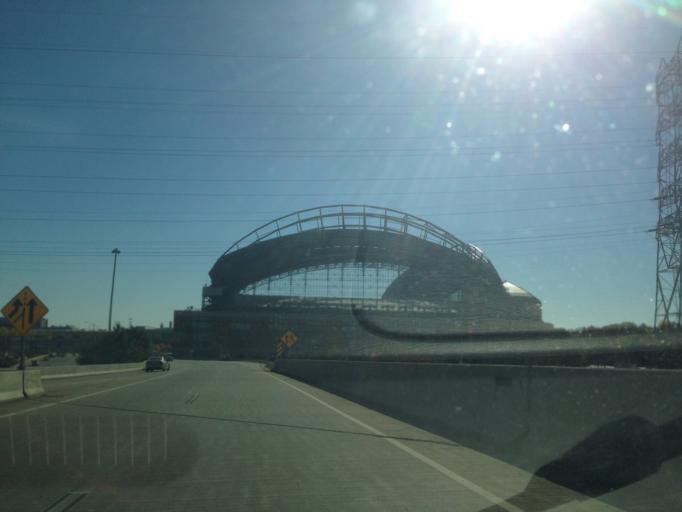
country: US
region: Wisconsin
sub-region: Milwaukee County
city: West Milwaukee
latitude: 43.0325
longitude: -87.9706
